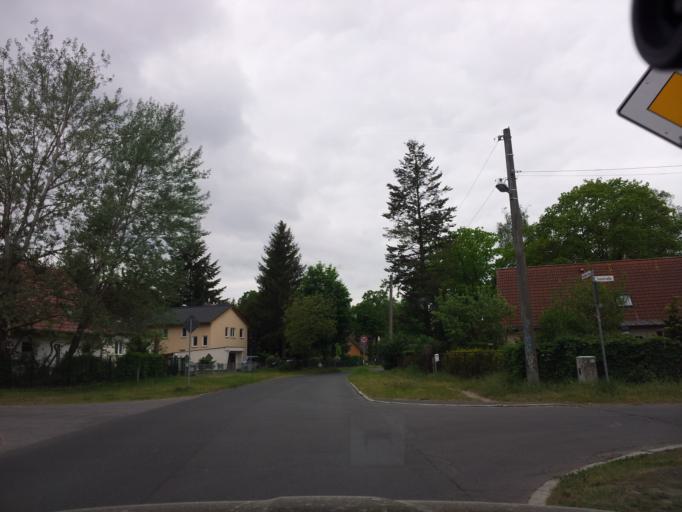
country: DE
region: Brandenburg
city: Falkensee
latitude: 52.5792
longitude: 13.0718
